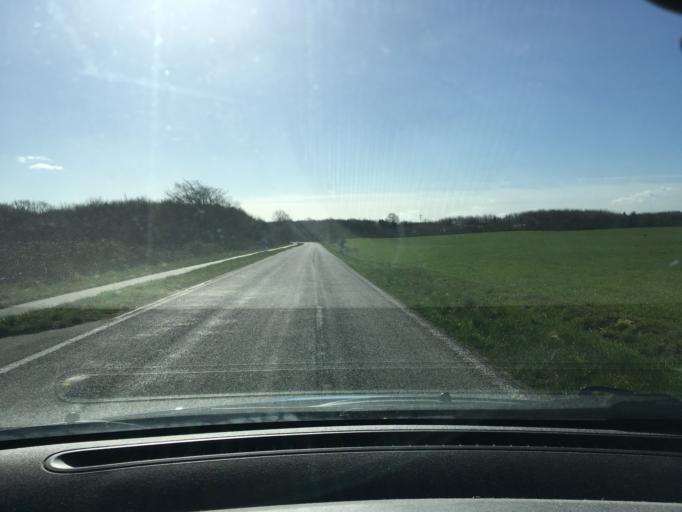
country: DE
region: Schleswig-Holstein
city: Borgwedel
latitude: 54.4981
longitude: 9.6493
